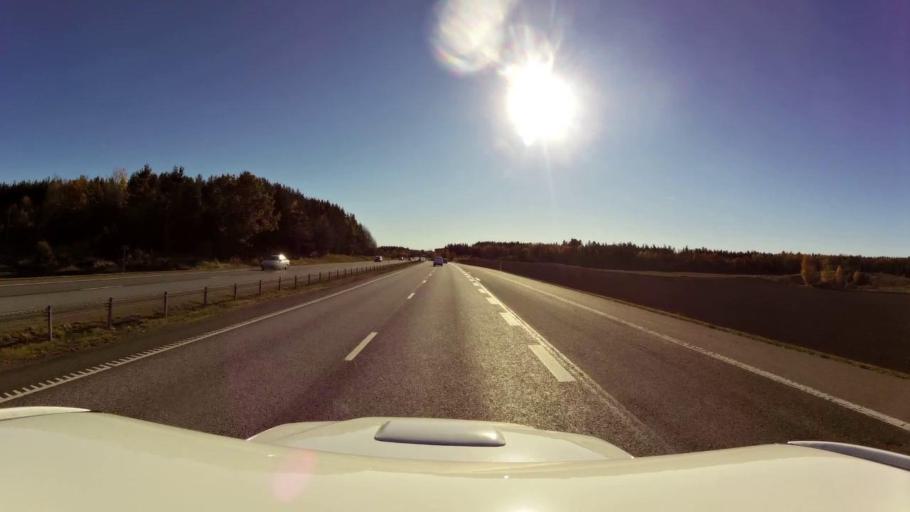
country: SE
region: OEstergoetland
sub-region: Linkopings Kommun
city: Malmslatt
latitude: 58.4216
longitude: 15.5394
